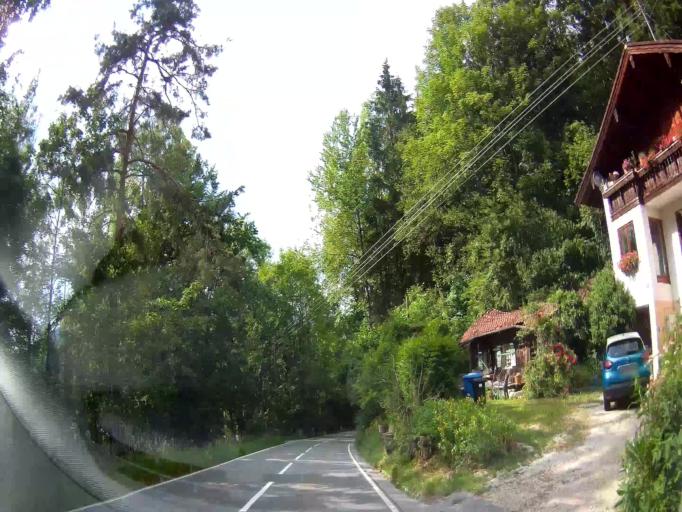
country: DE
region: Bavaria
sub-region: Upper Bavaria
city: Marktschellenberg
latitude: 47.6462
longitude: 13.0584
